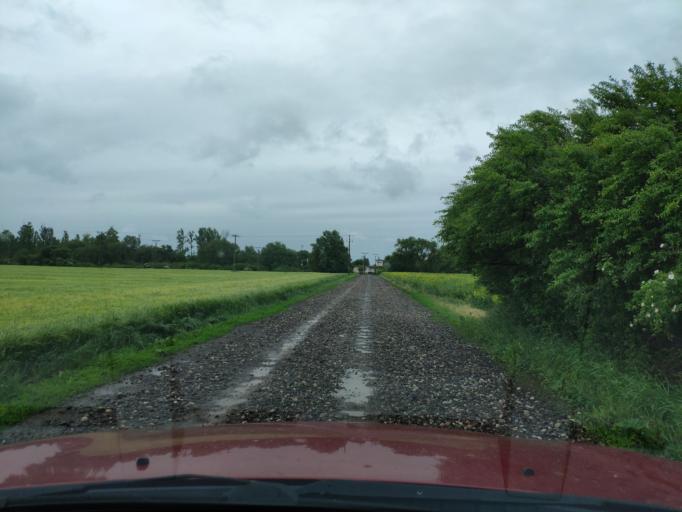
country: SK
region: Kosicky
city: Cierna nad Tisou
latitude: 48.4264
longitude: 22.0816
